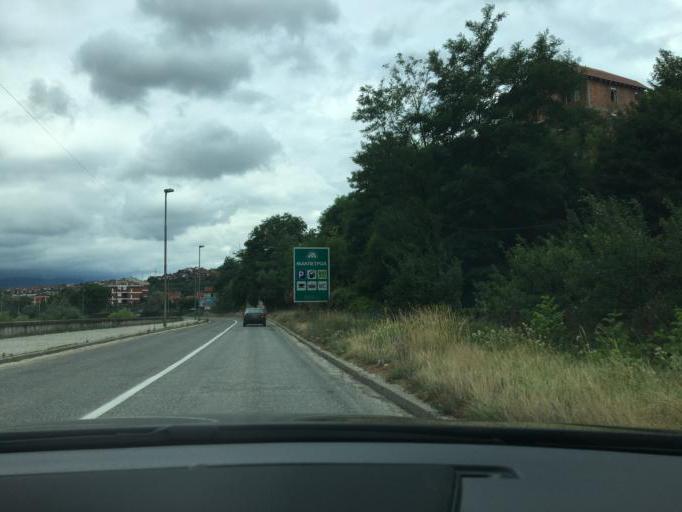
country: MK
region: Kriva Palanka
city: Kriva Palanka
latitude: 42.2117
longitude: 22.3433
